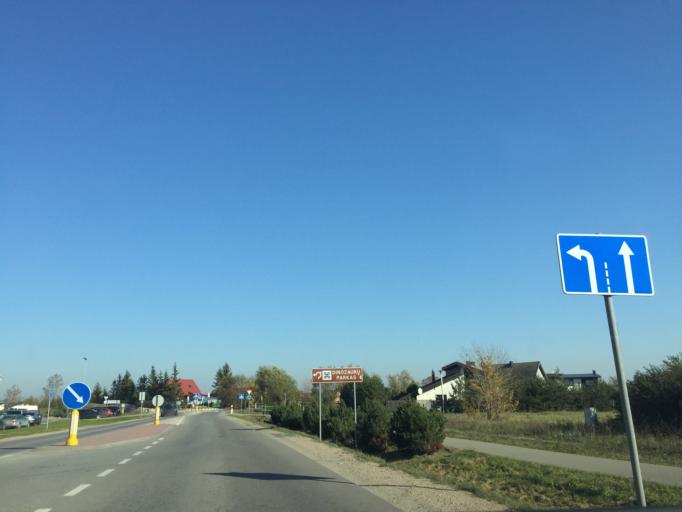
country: LT
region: Klaipedos apskritis
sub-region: Klaipeda
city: Klaipeda
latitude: 55.7358
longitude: 21.1917
